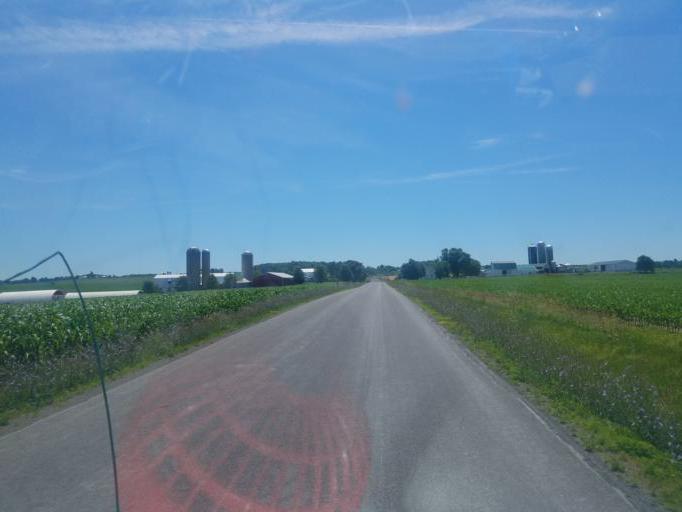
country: US
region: New York
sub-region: Yates County
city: Penn Yan
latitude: 42.6466
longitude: -77.0176
